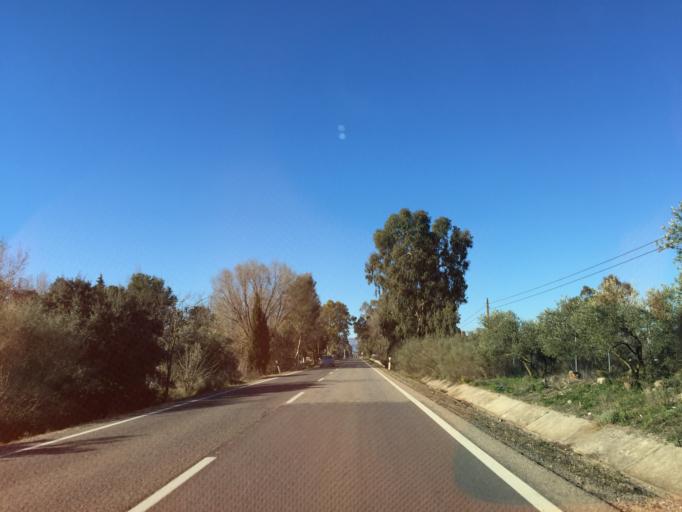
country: ES
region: Andalusia
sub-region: Provincia de Malaga
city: Arriate
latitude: 36.7877
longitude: -5.1117
